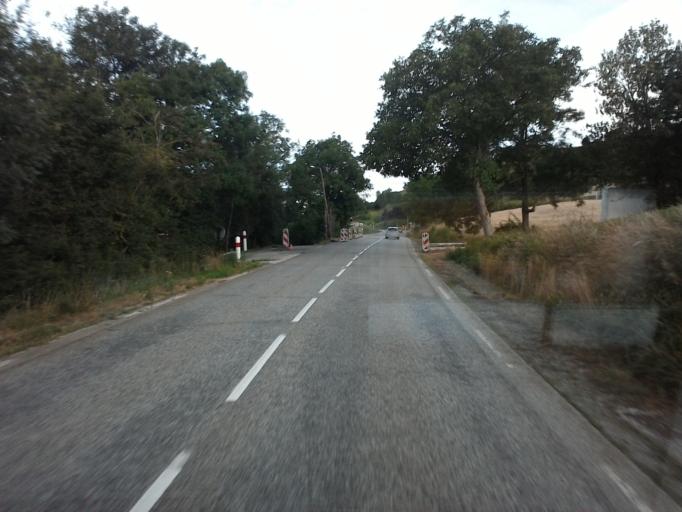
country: FR
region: Rhone-Alpes
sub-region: Departement de l'Isere
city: La Mure
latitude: 44.8677
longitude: 5.8464
